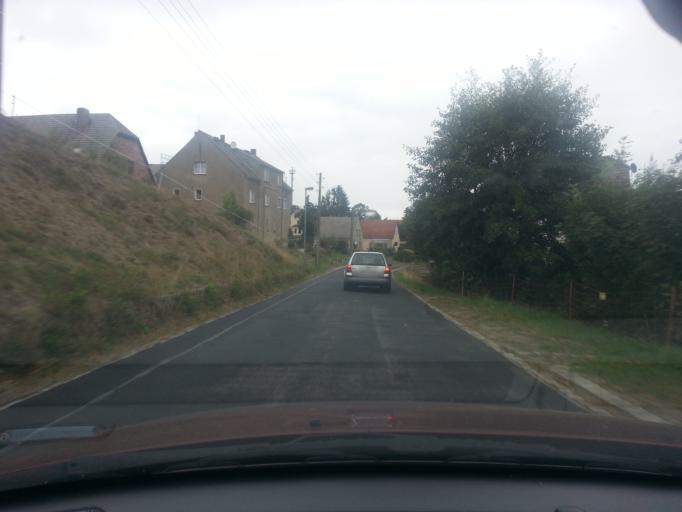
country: DE
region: Saxony
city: Schonau-Berzdorf
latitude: 51.0954
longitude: 14.8677
